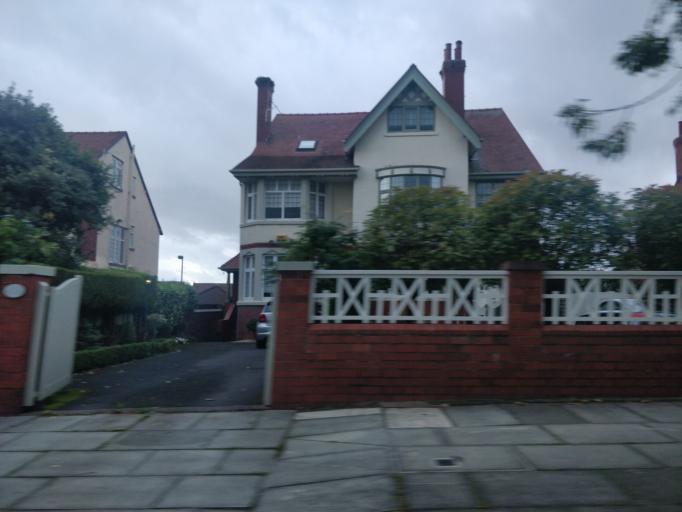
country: GB
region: England
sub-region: Sefton
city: Southport
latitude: 53.6592
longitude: -2.9826
